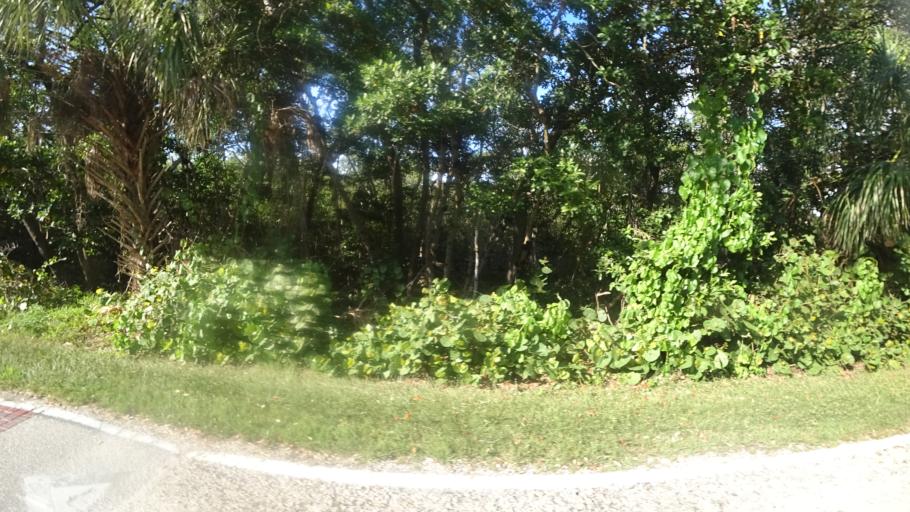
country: US
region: Florida
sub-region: Manatee County
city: West Bradenton
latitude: 27.5337
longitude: -82.6404
